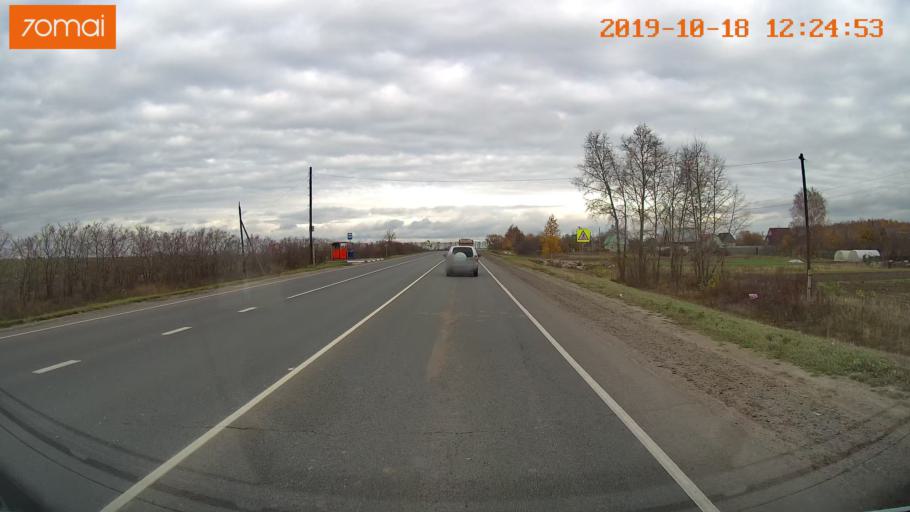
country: RU
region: Rjazan
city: Rybnoye
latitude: 54.5436
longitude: 39.5157
